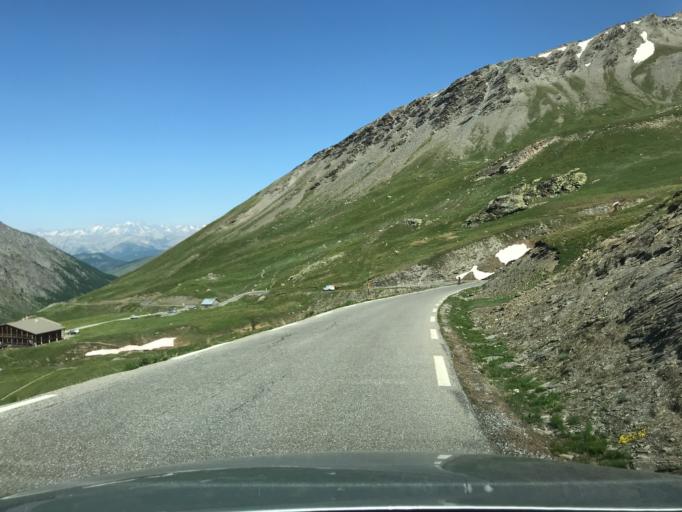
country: IT
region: Piedmont
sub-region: Provincia di Cuneo
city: Pontechianale
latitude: 44.6901
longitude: 6.9742
